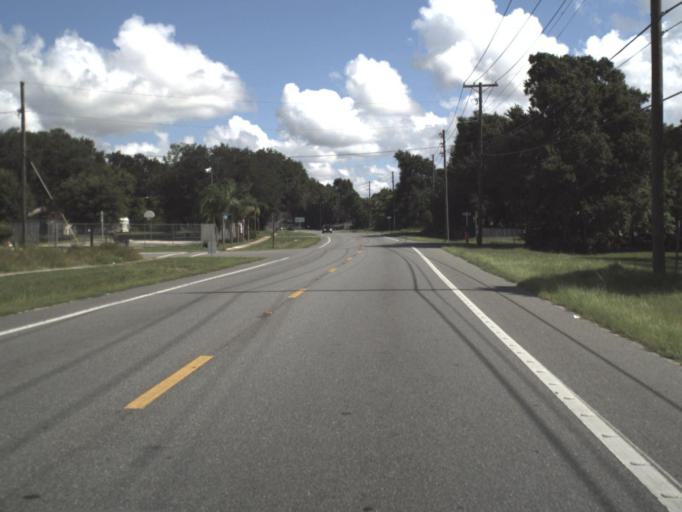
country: US
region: Florida
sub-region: Polk County
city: Davenport
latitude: 28.1657
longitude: -81.5989
